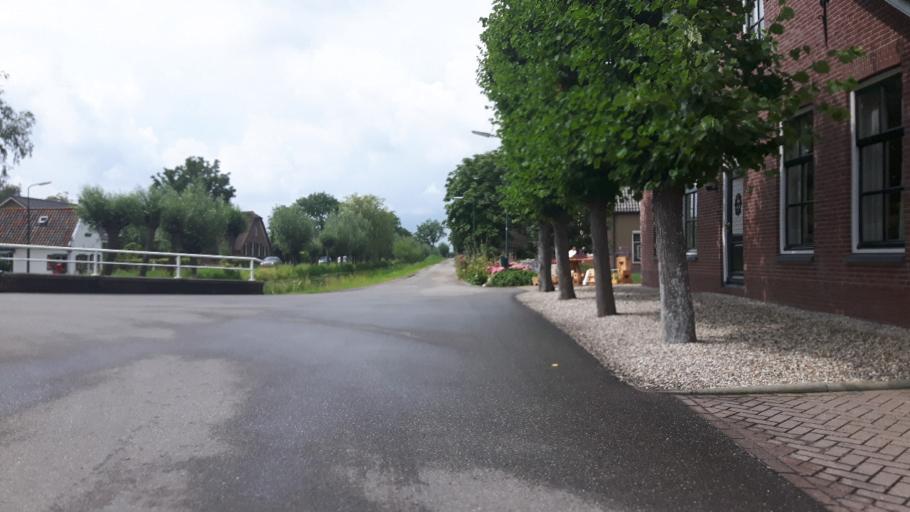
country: NL
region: Utrecht
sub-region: Gemeente Oudewater
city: Oudewater
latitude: 51.9861
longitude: 4.8763
